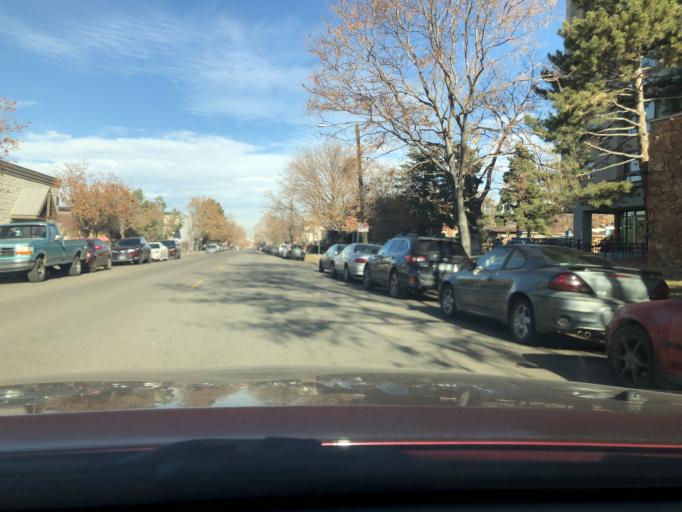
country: US
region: Colorado
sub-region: Denver County
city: Denver
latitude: 39.7478
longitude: -104.9771
